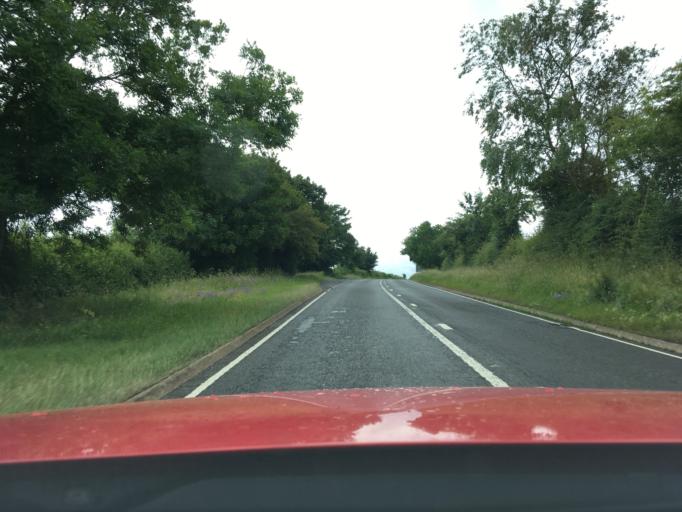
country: GB
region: England
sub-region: Warwickshire
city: Wellesbourne Mountford
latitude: 52.1261
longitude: -1.6030
